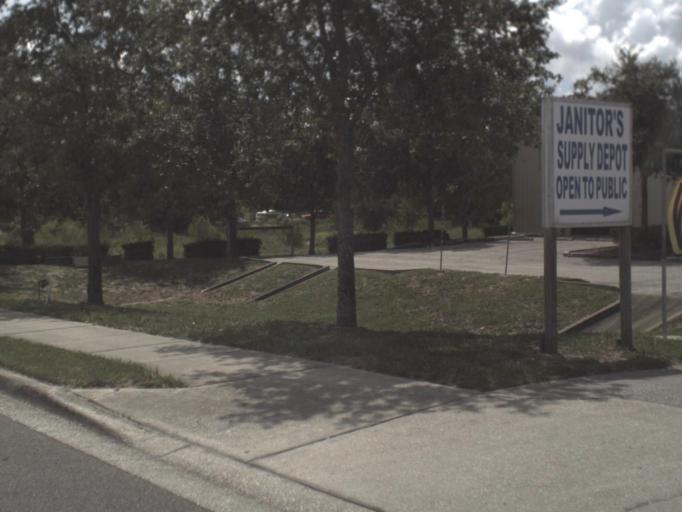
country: US
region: Florida
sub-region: Pasco County
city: Bayonet Point
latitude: 28.3311
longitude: -82.6471
